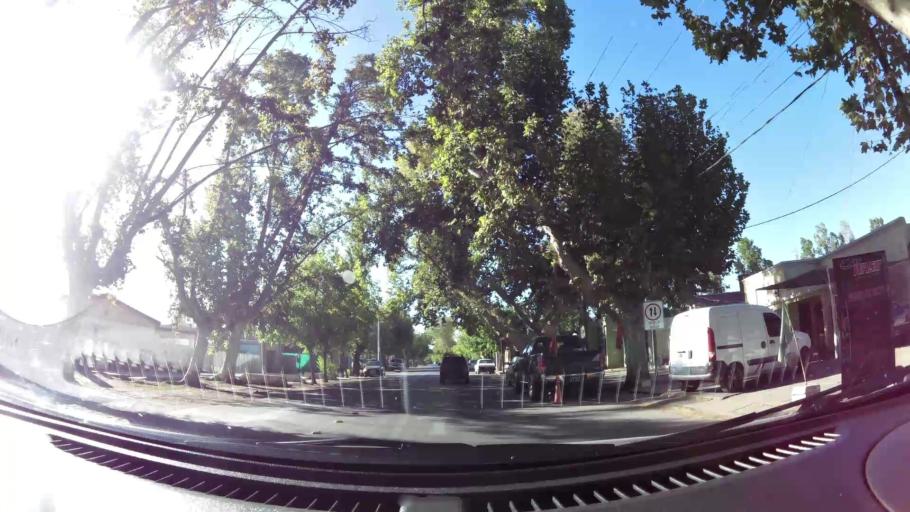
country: AR
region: San Juan
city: Villa Krause
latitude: -31.5690
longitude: -68.5198
